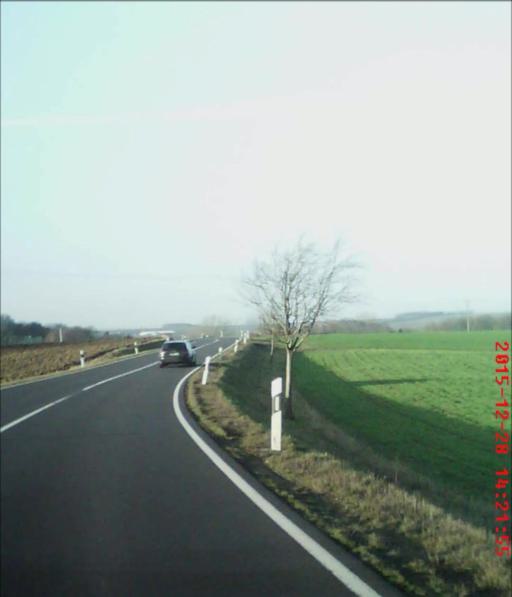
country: DE
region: Thuringia
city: Niederrossla
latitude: 51.0456
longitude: 11.4741
